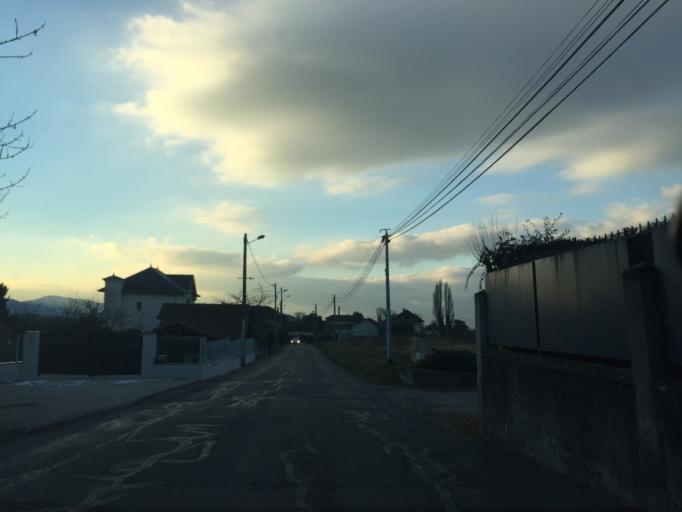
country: FR
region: Rhone-Alpes
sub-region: Departement de la Savoie
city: Tresserve
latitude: 45.6657
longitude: 5.8997
